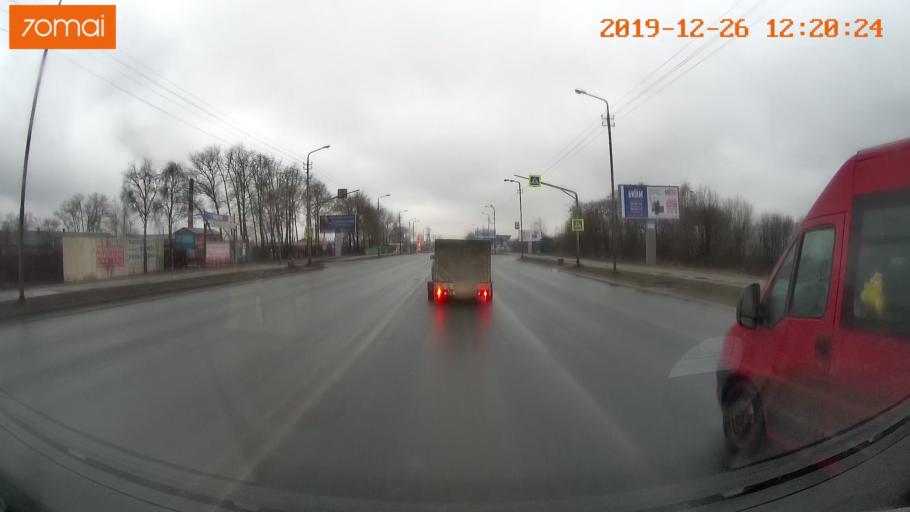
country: RU
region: Vologda
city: Tonshalovo
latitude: 59.1586
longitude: 37.9325
